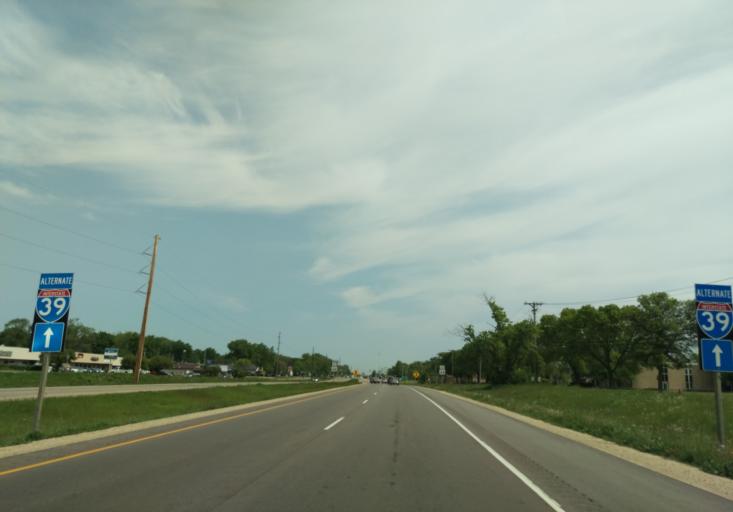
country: US
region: Wisconsin
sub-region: Dane County
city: Monona
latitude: 43.0688
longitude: -89.3093
